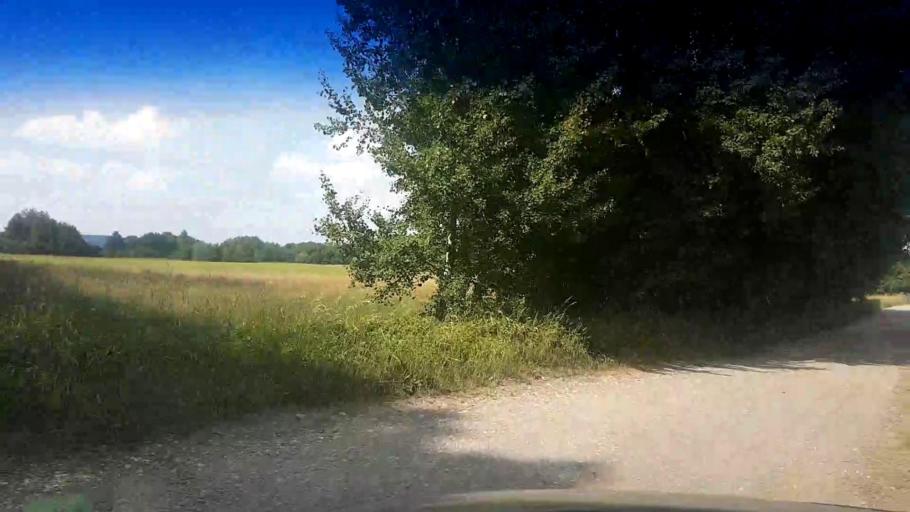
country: DE
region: Bavaria
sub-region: Upper Franconia
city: Kemmern
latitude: 49.9507
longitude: 10.8623
